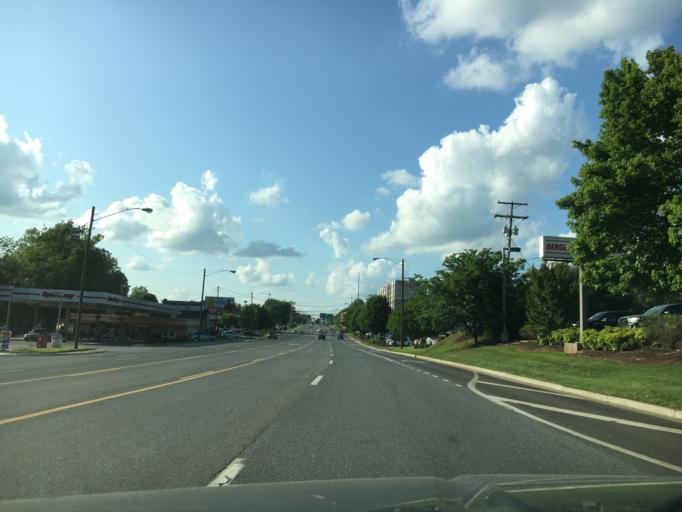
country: US
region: Virginia
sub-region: City of Lynchburg
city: West Lynchburg
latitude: 37.3591
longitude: -79.1807
